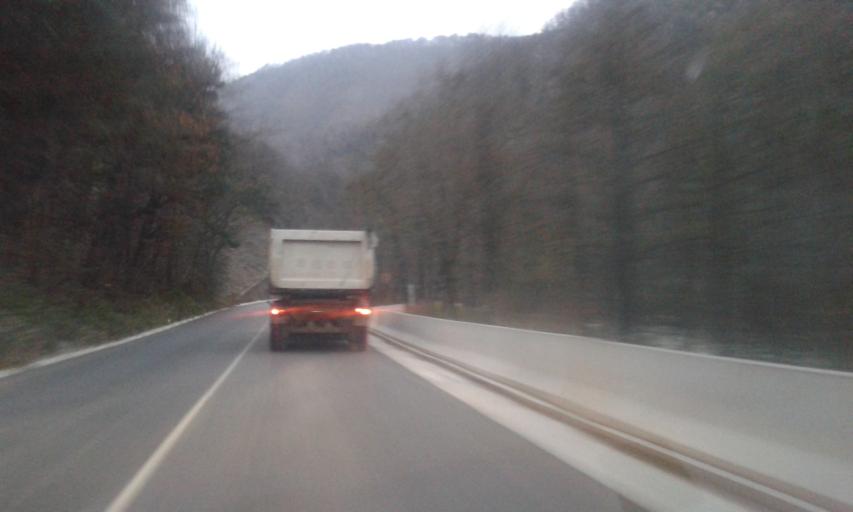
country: RO
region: Gorj
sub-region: Comuna Bumbesti-Jiu
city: Bumbesti-Jiu
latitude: 45.2082
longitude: 23.3747
